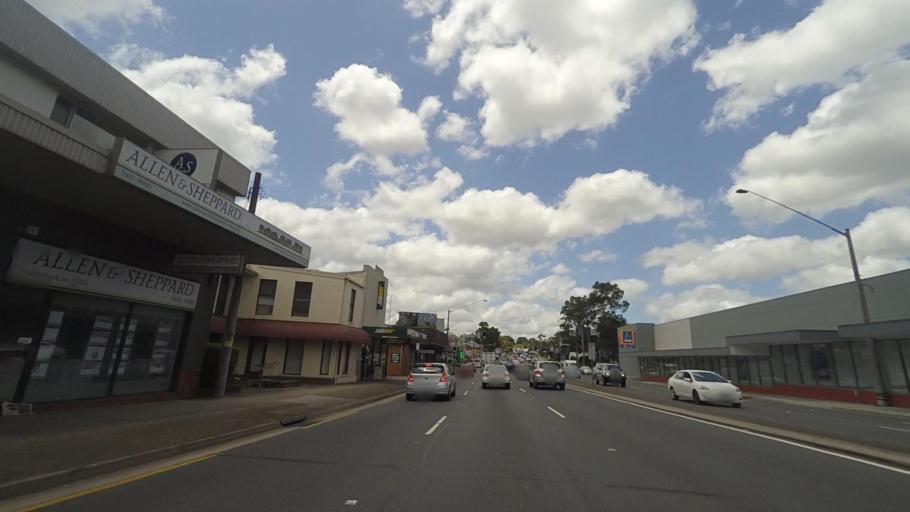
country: AU
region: New South Wales
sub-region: Hornsby Shire
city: Pennant Hills
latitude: -33.7319
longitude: 151.0794
